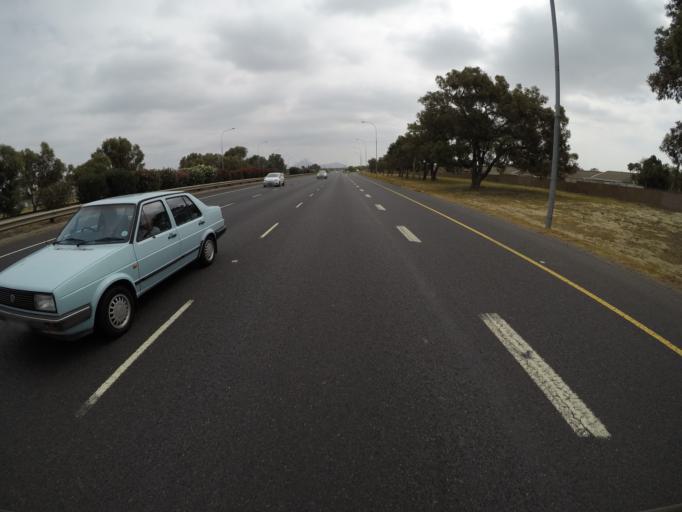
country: ZA
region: Western Cape
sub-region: City of Cape Town
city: Sunset Beach
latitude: -33.8895
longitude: 18.5585
